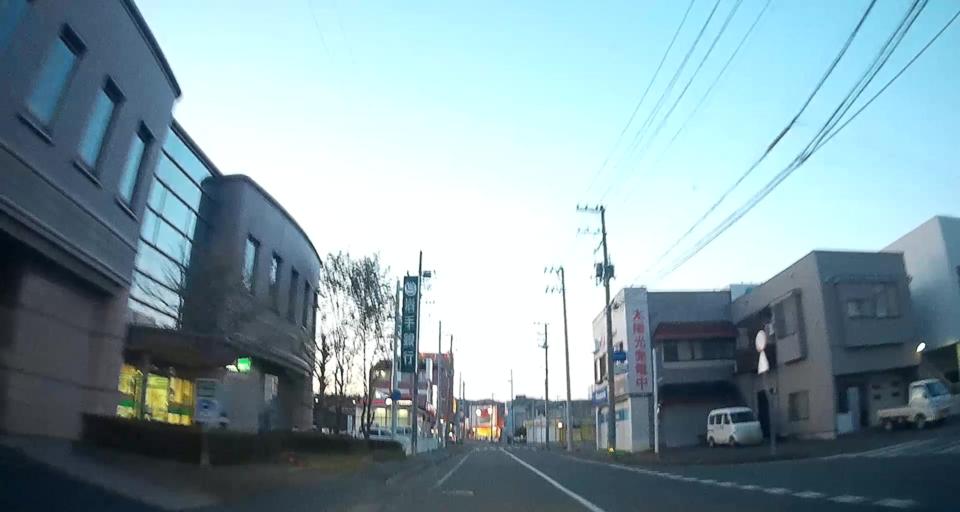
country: JP
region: Aomori
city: Hachinohe
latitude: 40.1899
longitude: 141.7721
